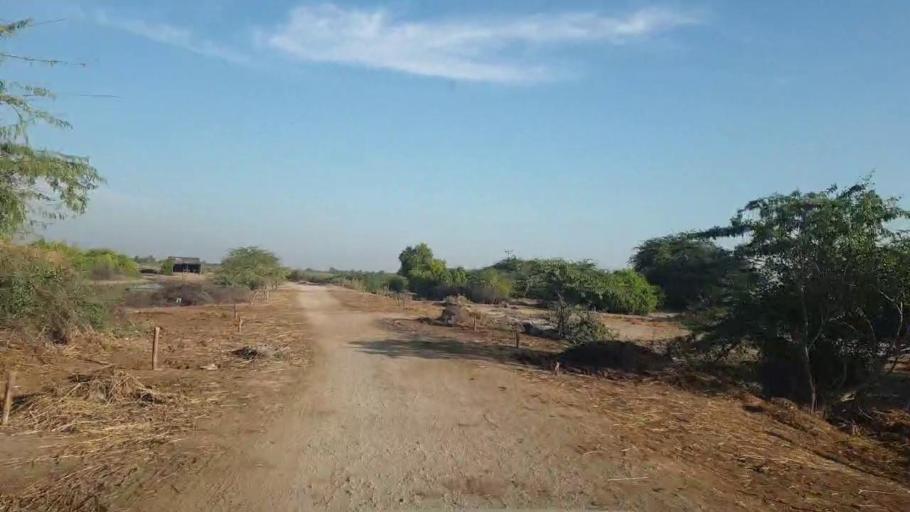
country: PK
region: Sindh
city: Talhar
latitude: 24.8165
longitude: 68.8400
